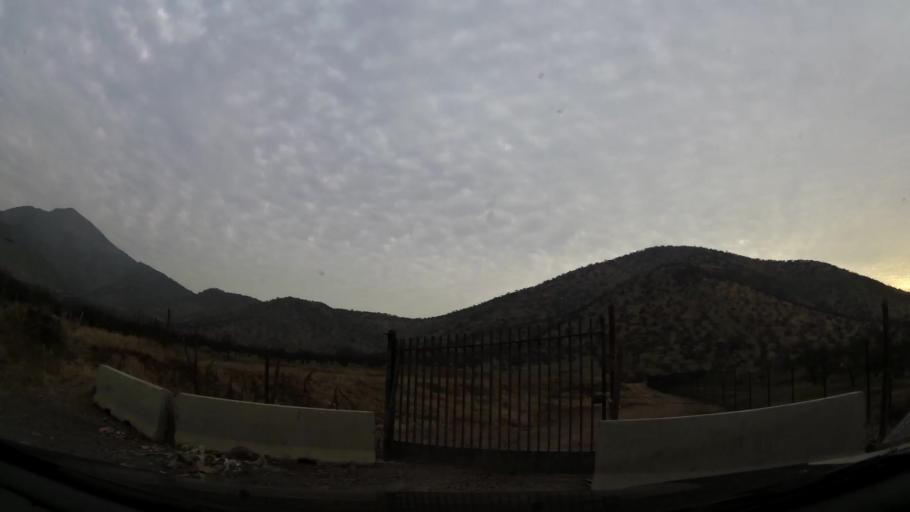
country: CL
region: Santiago Metropolitan
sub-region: Provincia de Chacabuco
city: Chicureo Abajo
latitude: -33.3243
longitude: -70.6504
